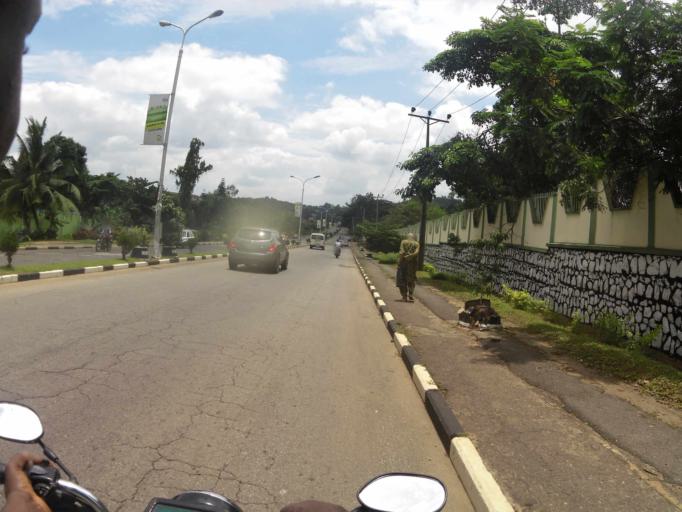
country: NG
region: Oyo
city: Ibadan
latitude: 7.4069
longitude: 3.9050
